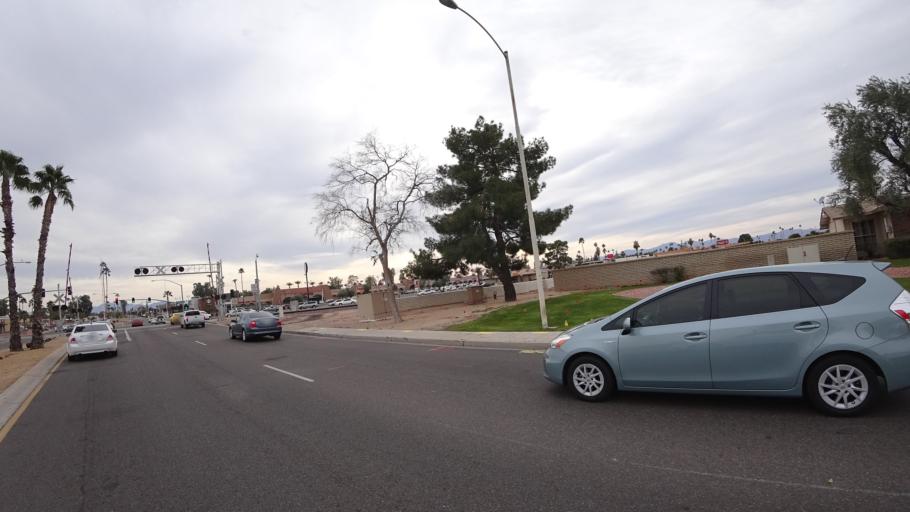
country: US
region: Arizona
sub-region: Maricopa County
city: Youngtown
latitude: 33.6035
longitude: -112.2900
